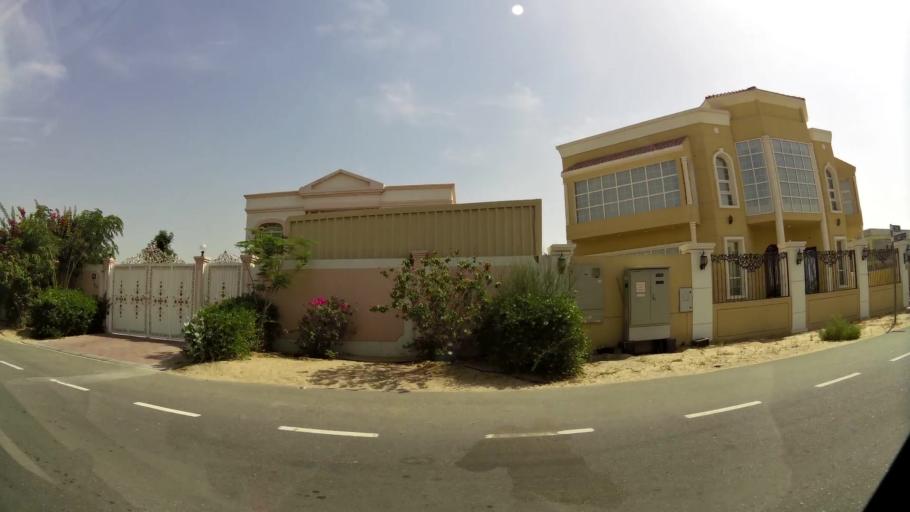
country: AE
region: Ash Shariqah
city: Sharjah
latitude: 25.2026
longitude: 55.4117
